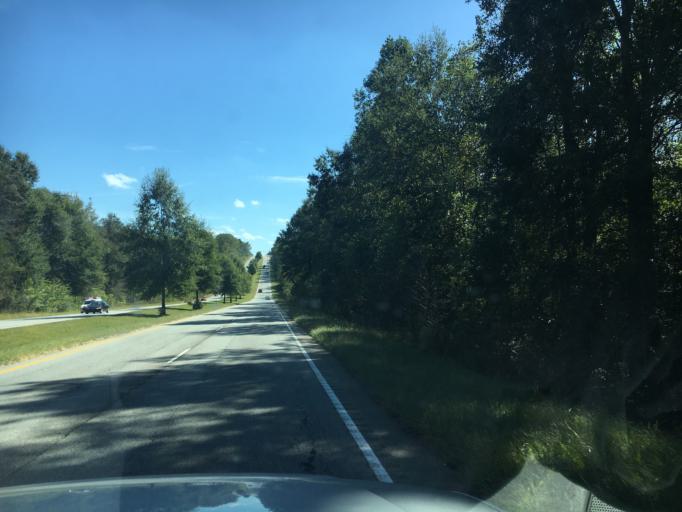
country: US
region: South Carolina
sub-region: Spartanburg County
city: Fairforest
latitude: 34.9397
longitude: -82.0447
